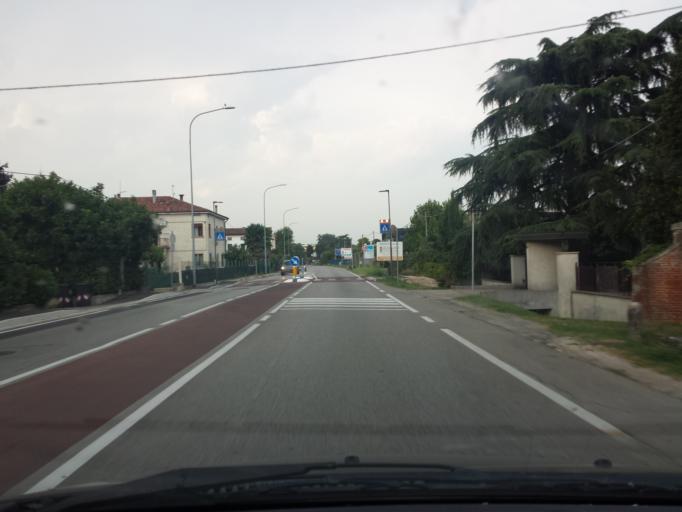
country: IT
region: Veneto
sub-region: Provincia di Vicenza
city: Monticello Conte Otto
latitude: 45.5847
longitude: 11.5553
